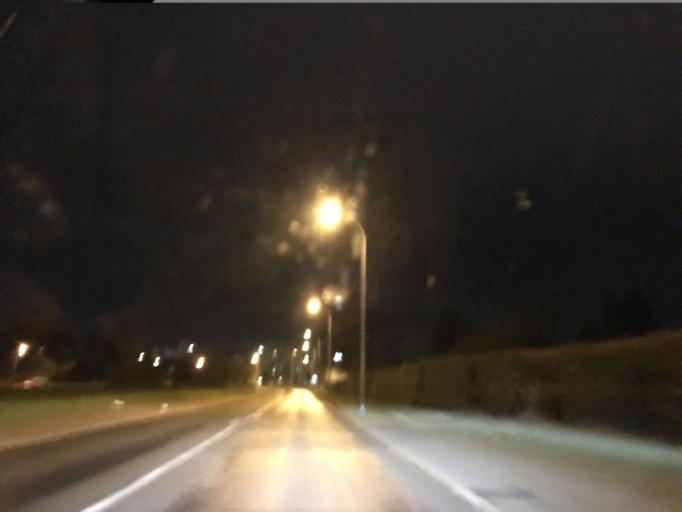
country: FR
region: Auvergne
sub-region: Departement de l'Allier
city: Vichy
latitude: 46.1116
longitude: 3.4206
